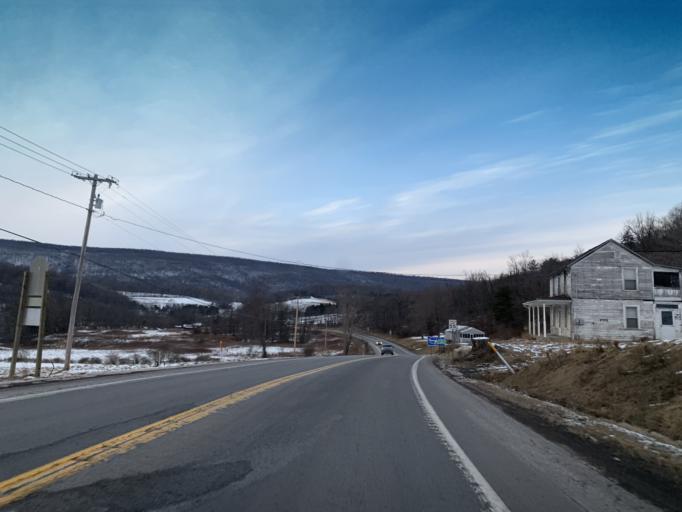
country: US
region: Maryland
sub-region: Allegany County
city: Cumberland
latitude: 39.7227
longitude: -78.7062
